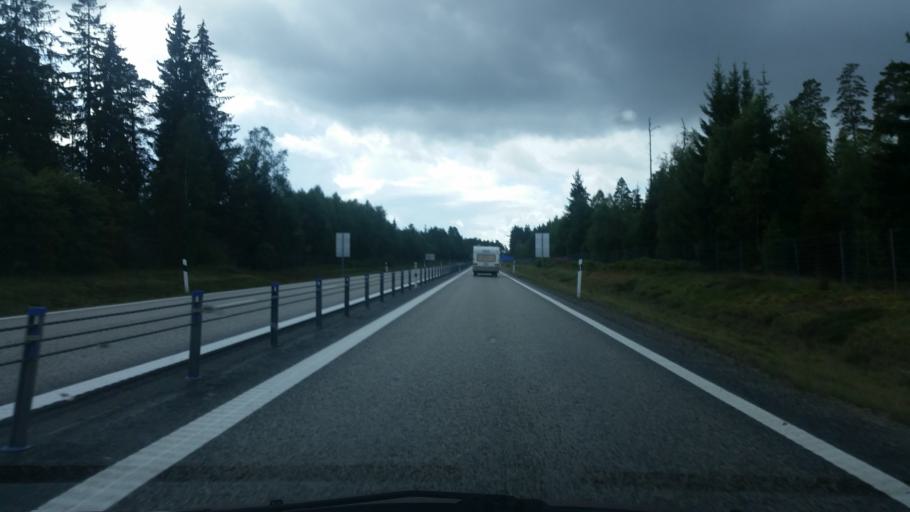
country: SE
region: Joenkoeping
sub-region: Gislaveds Kommun
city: Gislaved
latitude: 57.3345
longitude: 13.5484
